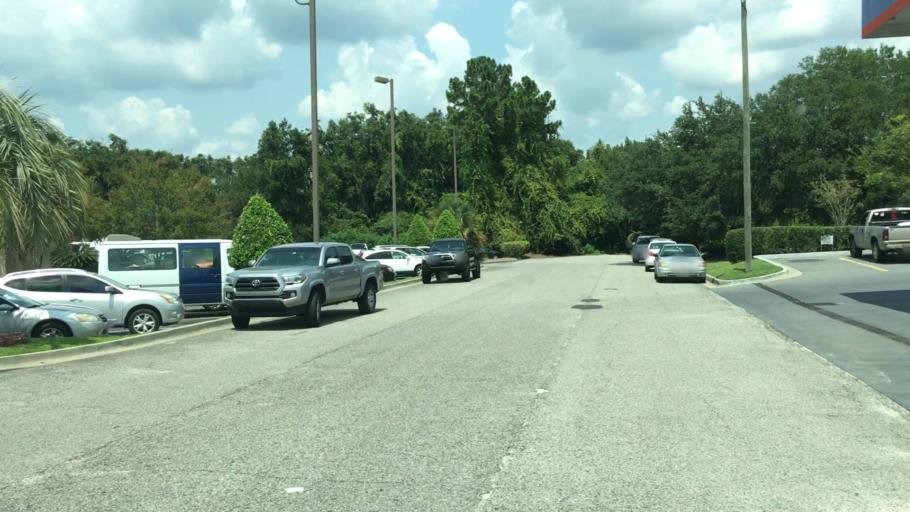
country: US
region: Georgia
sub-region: Lowndes County
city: Valdosta
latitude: 30.6819
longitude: -83.2192
